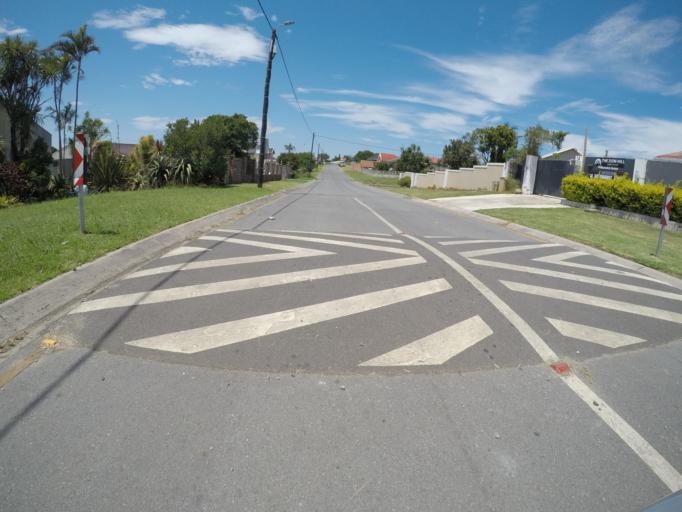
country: ZA
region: Eastern Cape
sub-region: Buffalo City Metropolitan Municipality
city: East London
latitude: -33.0315
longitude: 27.8512
